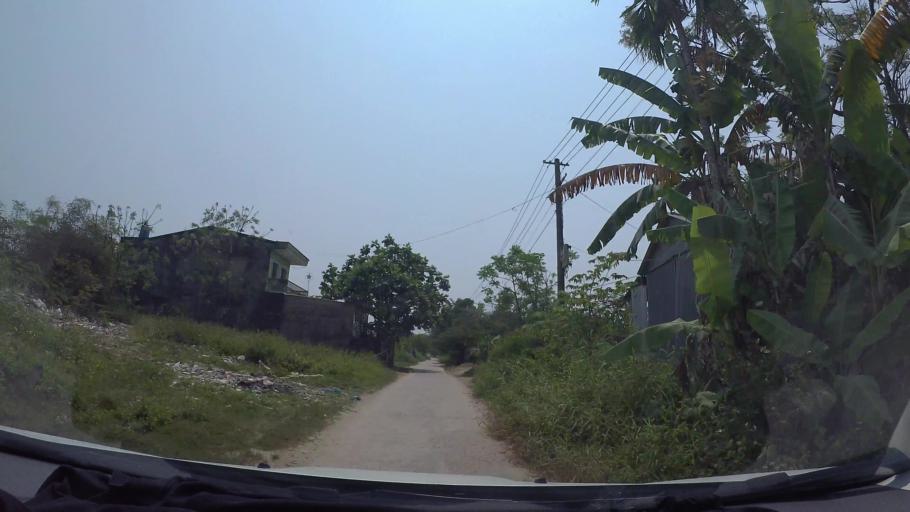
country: VN
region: Da Nang
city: Cam Le
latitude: 16.0201
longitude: 108.2235
